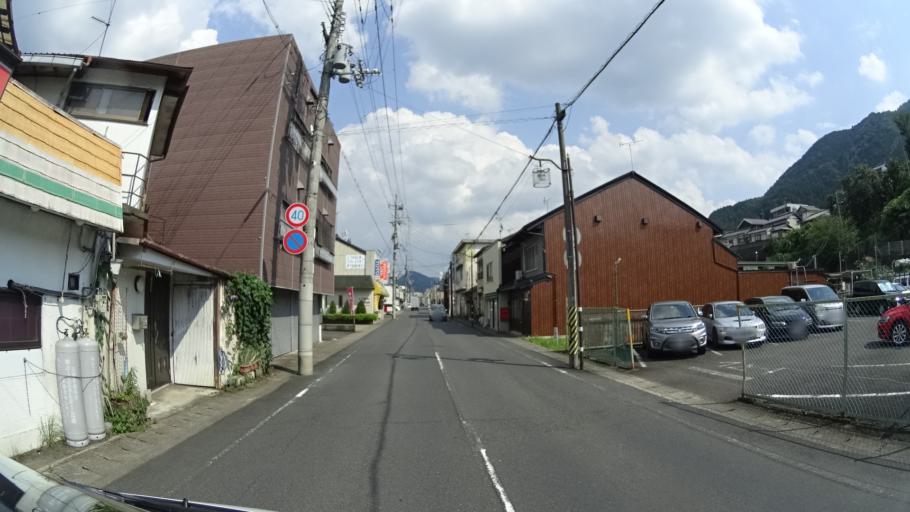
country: JP
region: Kyoto
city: Ayabe
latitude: 35.3005
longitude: 135.2500
